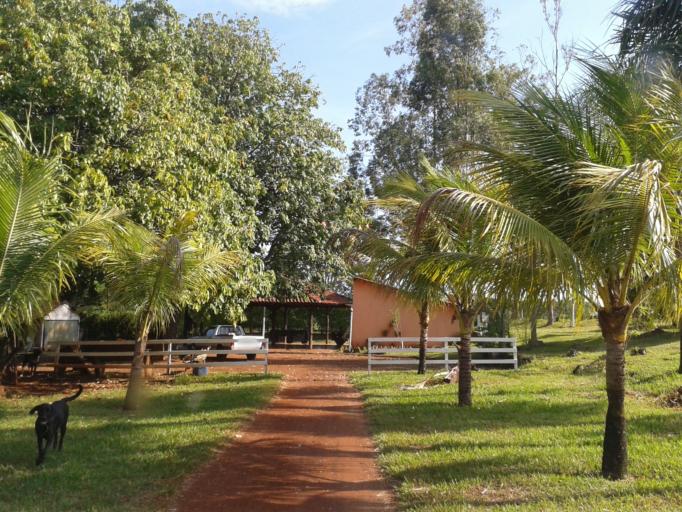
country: BR
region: Minas Gerais
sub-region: Centralina
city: Centralina
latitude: -18.7076
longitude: -49.1884
